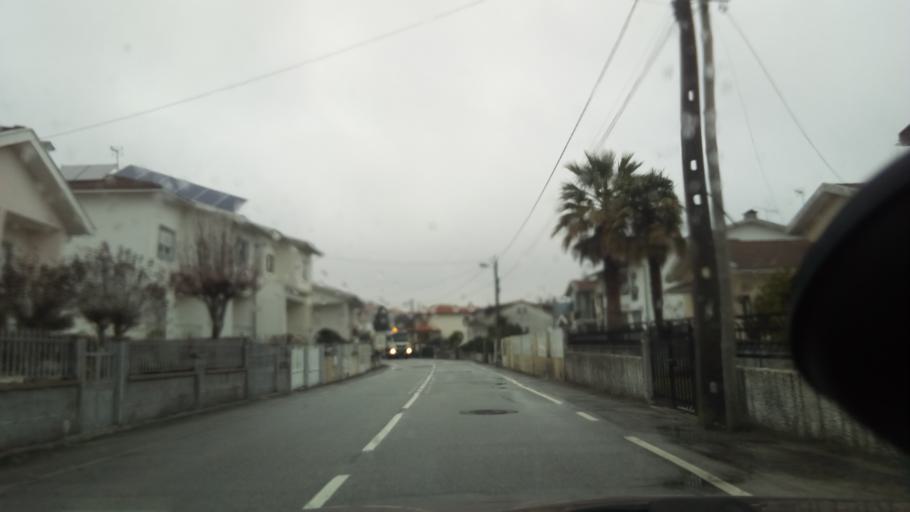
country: PT
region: Viseu
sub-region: Viseu
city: Rio de Loba
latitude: 40.6516
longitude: -7.8730
